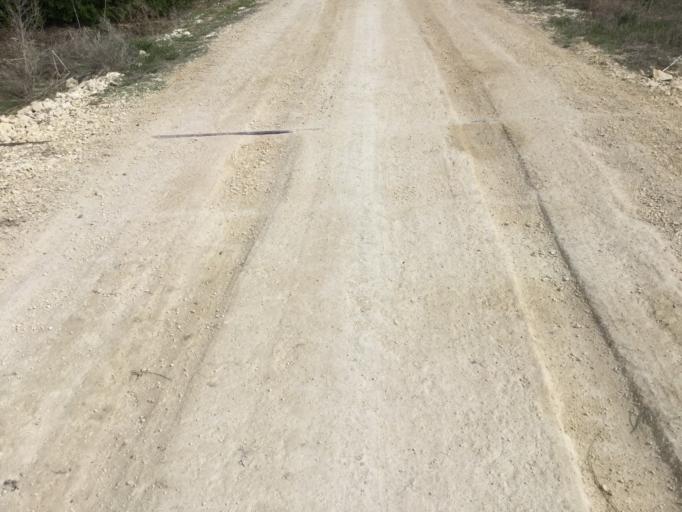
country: US
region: Kansas
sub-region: Osborne County
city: Osborne
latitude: 39.4160
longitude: -98.5268
